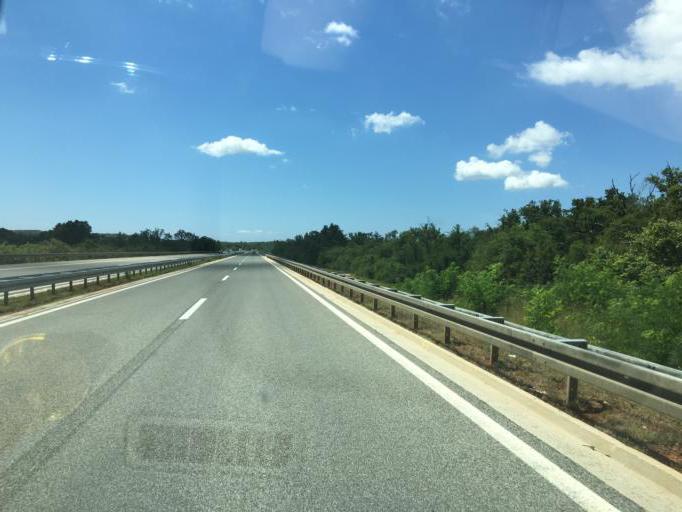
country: HR
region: Istarska
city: Vrsar
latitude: 45.1705
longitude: 13.7322
